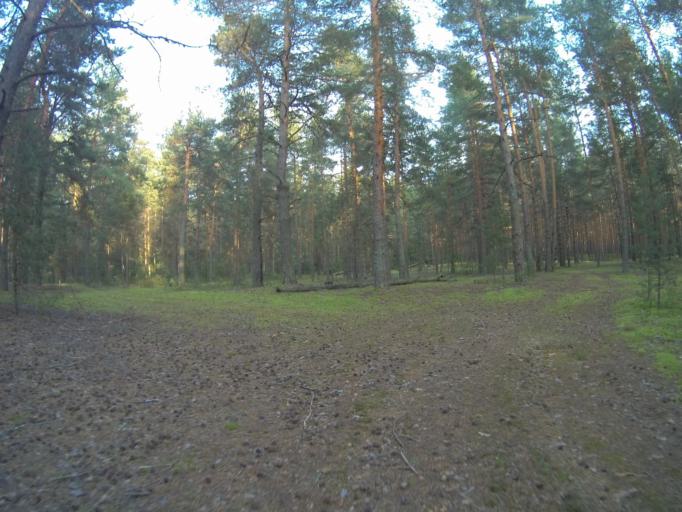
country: RU
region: Vladimir
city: Kommunar
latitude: 56.0802
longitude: 40.4361
